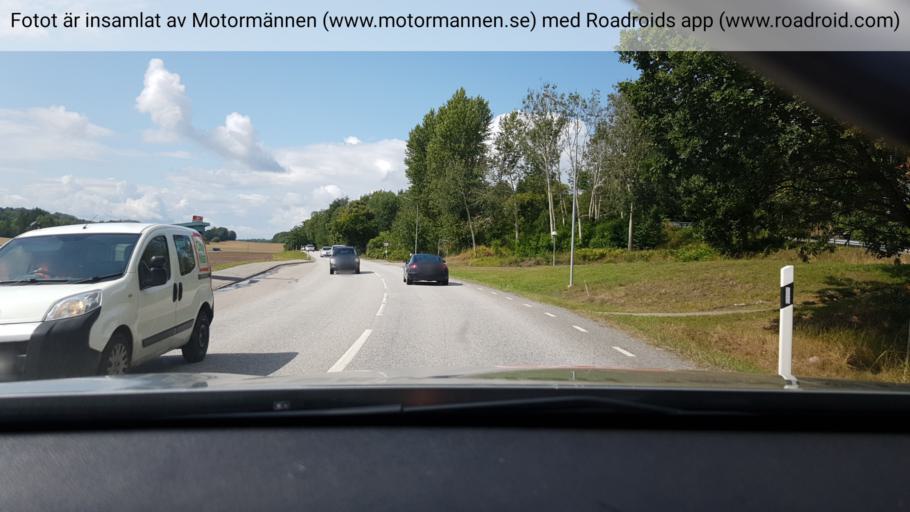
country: SE
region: Stockholm
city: Stenhamra
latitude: 59.2844
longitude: 17.7278
